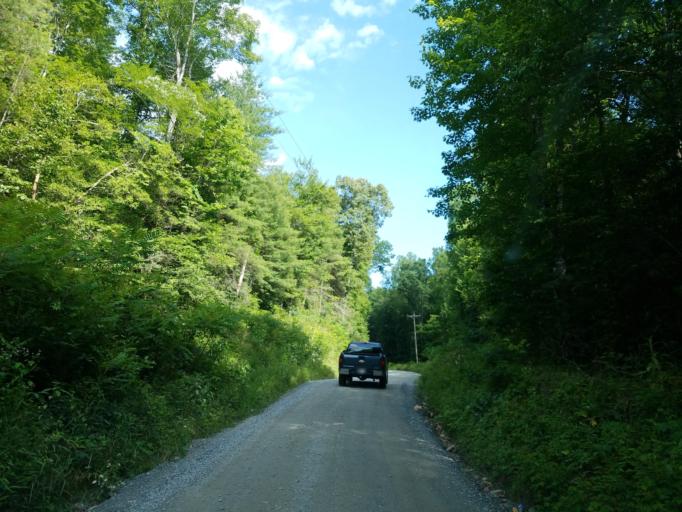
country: US
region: Georgia
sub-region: Fannin County
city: Blue Ridge
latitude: 34.7840
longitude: -84.2375
